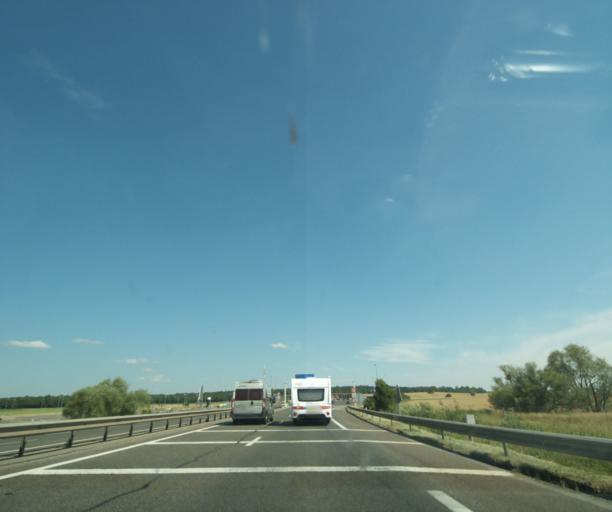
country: FR
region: Lorraine
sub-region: Departement de Meurthe-et-Moselle
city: Dommartin-les-Toul
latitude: 48.6261
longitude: 5.8844
